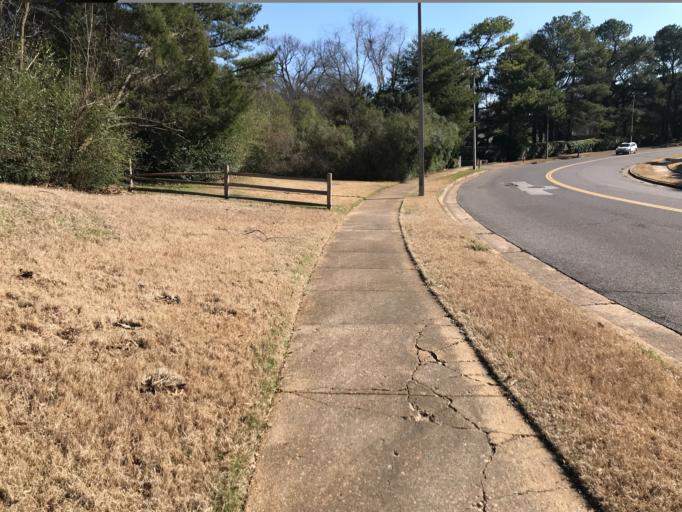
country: US
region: Tennessee
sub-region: Shelby County
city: Germantown
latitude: 35.1105
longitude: -89.8659
